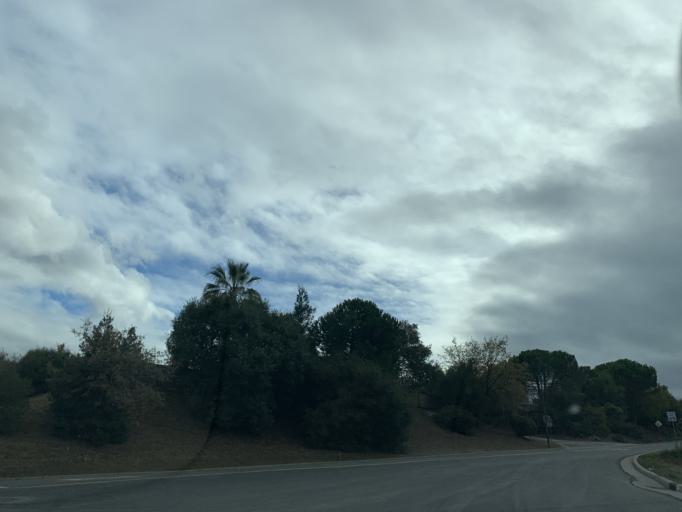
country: US
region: California
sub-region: Santa Clara County
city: Monte Sereno
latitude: 37.2590
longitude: -121.9843
